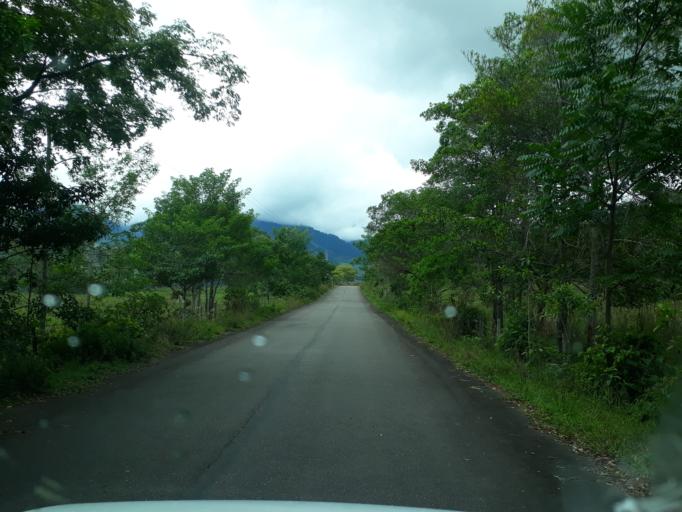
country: CO
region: Cundinamarca
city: Medina
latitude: 4.5798
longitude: -73.3606
